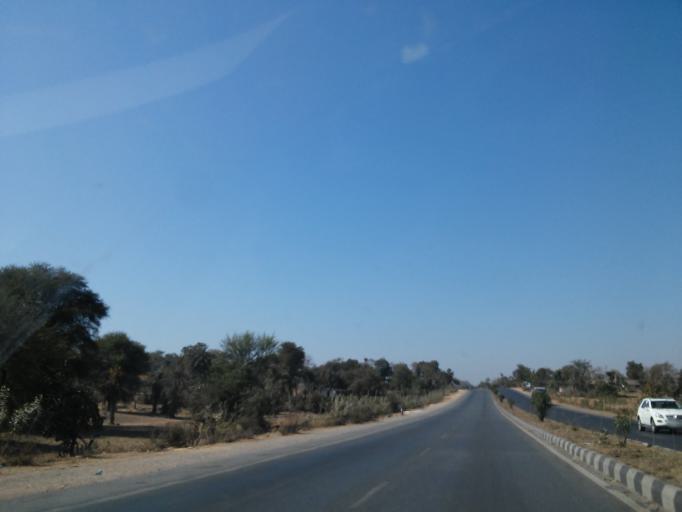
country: IN
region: Rajasthan
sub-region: Dungarpur
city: Dungarpur
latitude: 24.0018
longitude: 73.6490
